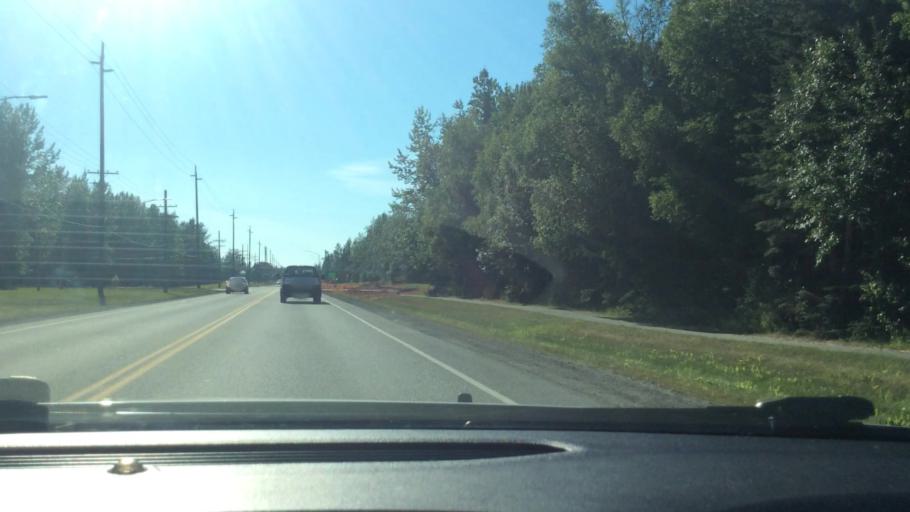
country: US
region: Alaska
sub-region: Anchorage Municipality
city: Elmendorf Air Force Base
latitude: 61.2314
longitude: -149.7526
